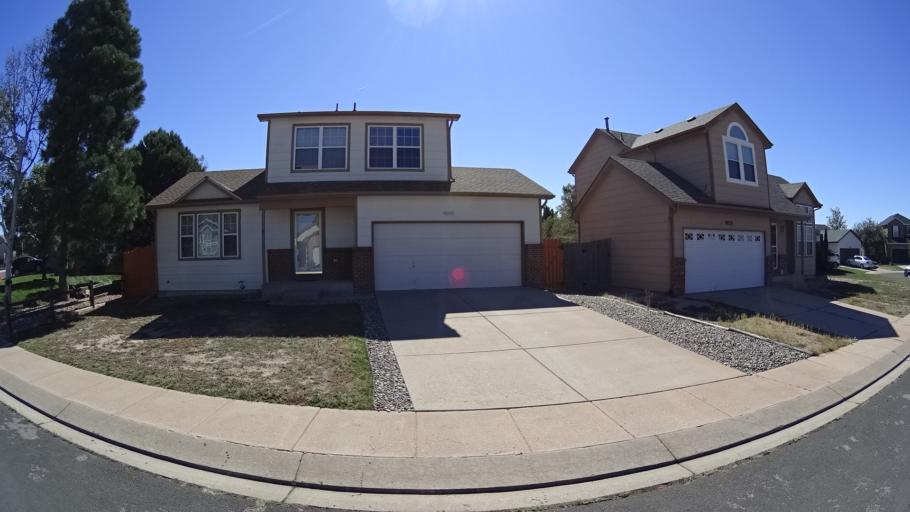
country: US
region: Colorado
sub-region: El Paso County
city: Stratmoor
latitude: 38.8091
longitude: -104.7389
